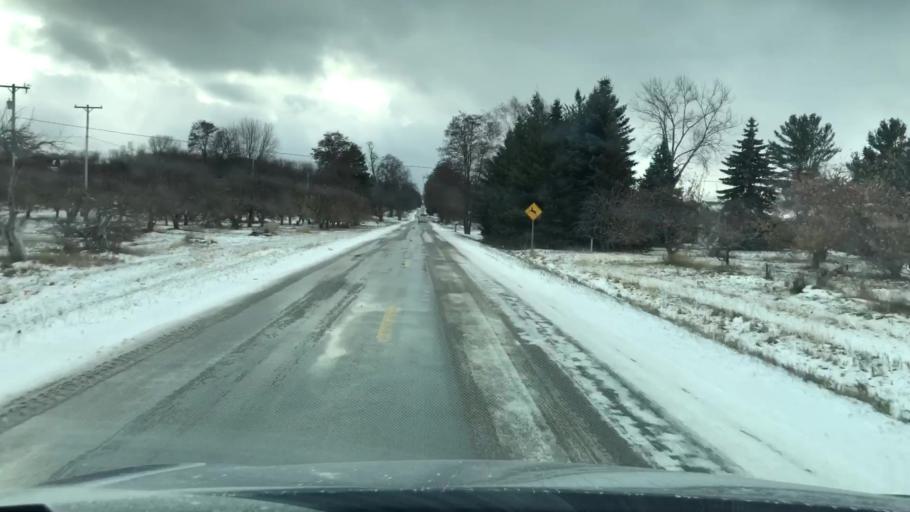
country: US
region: Michigan
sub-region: Antrim County
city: Elk Rapids
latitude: 44.9042
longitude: -85.5154
